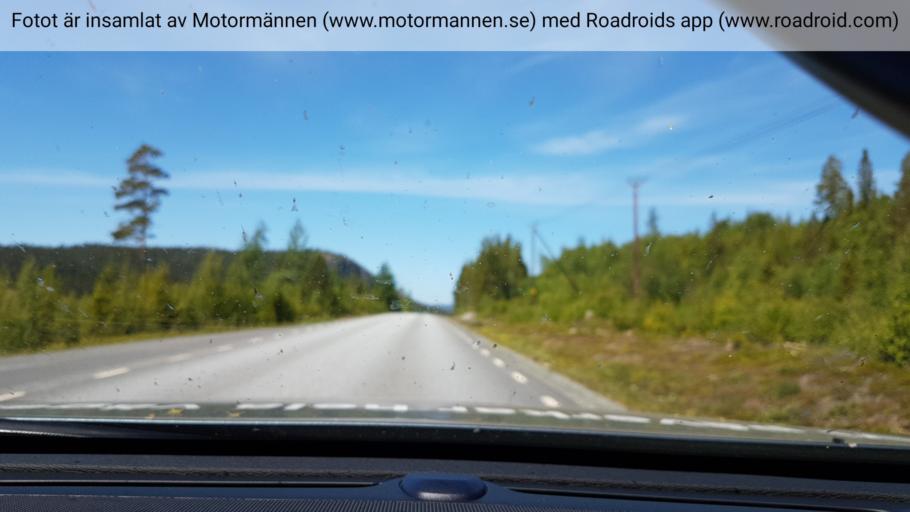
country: SE
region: Vaesterbotten
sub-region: Vilhelmina Kommun
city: Sjoberg
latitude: 64.6700
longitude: 15.6012
